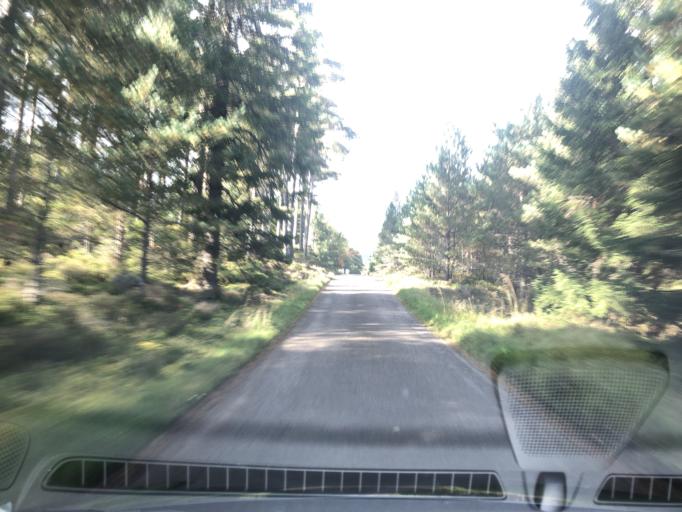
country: GB
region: Scotland
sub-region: Highland
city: Aviemore
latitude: 57.1139
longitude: -3.8934
